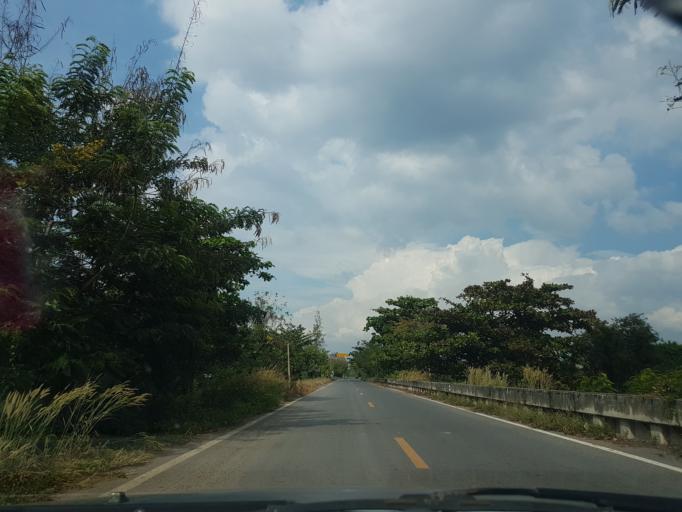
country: TH
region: Sara Buri
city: Nong Khae
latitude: 14.2434
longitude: 100.8913
